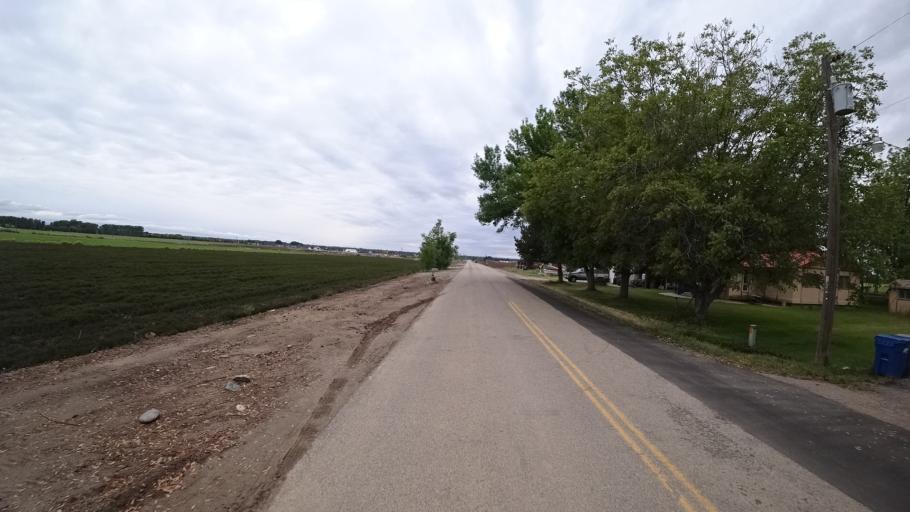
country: US
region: Idaho
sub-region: Ada County
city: Eagle
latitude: 43.7204
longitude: -116.4234
